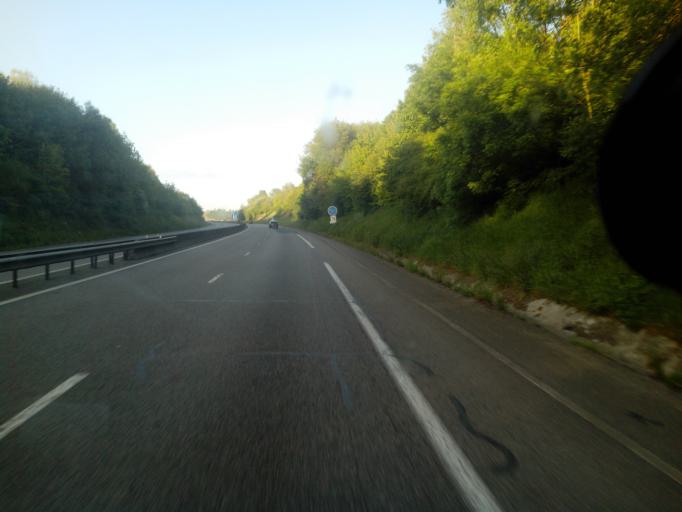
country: FR
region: Haute-Normandie
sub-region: Departement de la Seine-Maritime
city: Neufchatel-en-Bray
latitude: 49.7235
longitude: 1.4473
